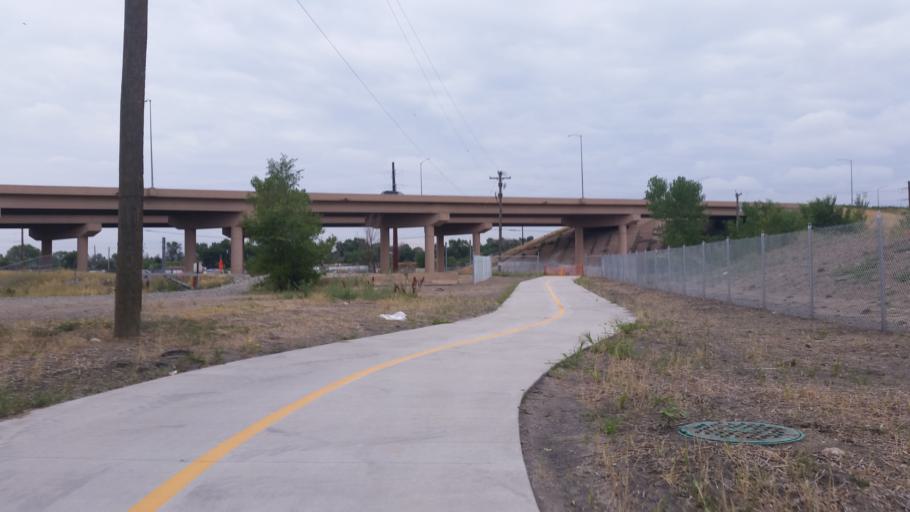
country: US
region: Colorado
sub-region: Adams County
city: Berkley
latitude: 39.8063
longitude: -105.0158
